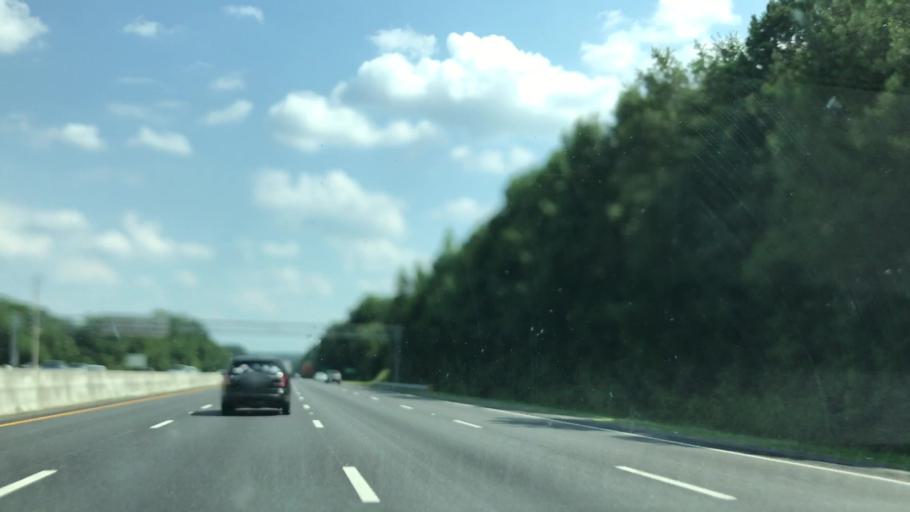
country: US
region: South Carolina
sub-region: York County
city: Rock Hill
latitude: 34.9609
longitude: -80.9814
